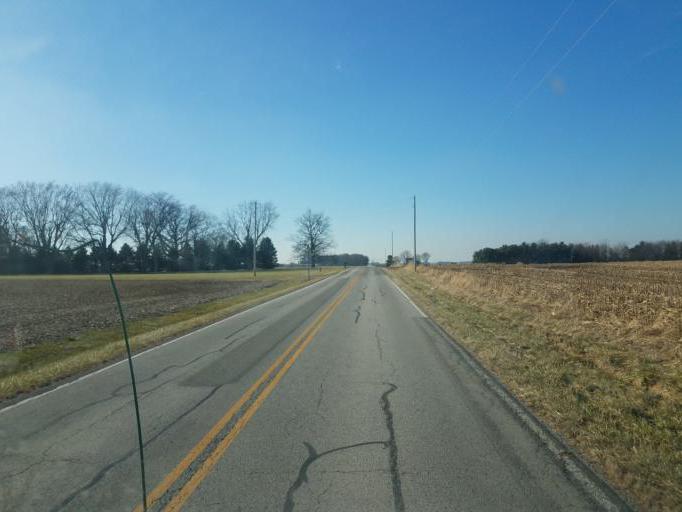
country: US
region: Ohio
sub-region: Marion County
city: Marion
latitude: 40.6442
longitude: -83.1987
